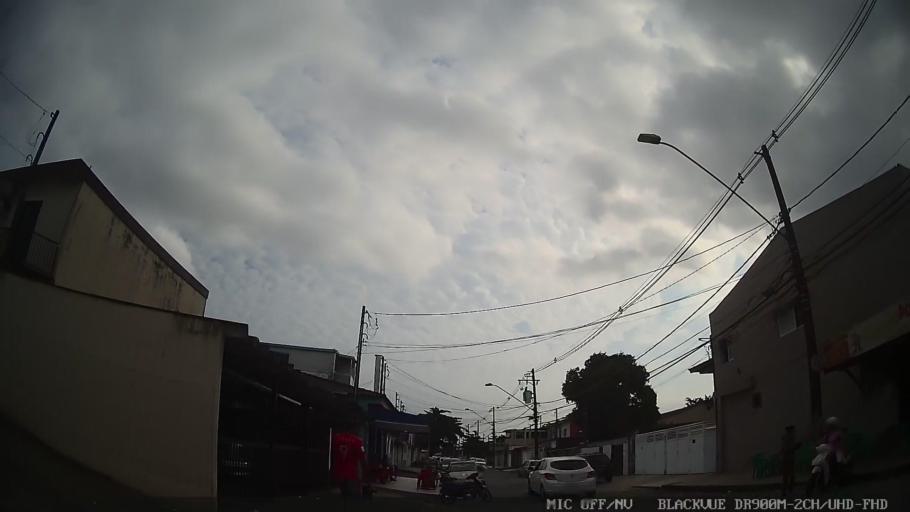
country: BR
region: Sao Paulo
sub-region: Guaruja
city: Guaruja
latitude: -23.9552
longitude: -46.2854
